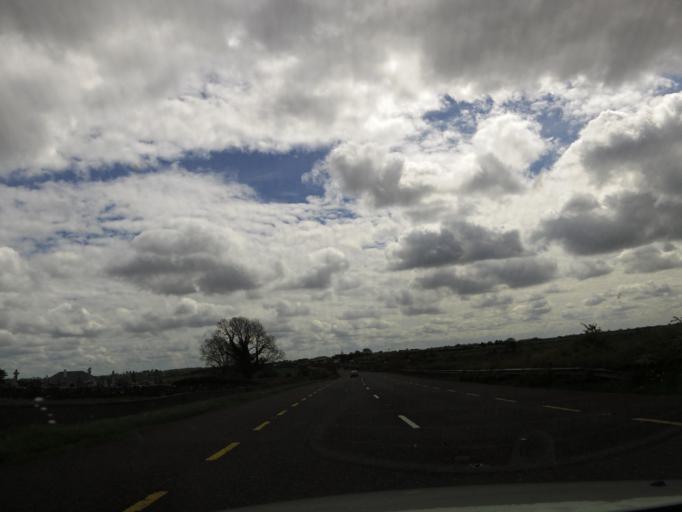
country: IE
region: Connaught
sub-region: County Galway
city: Tuam
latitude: 53.5904
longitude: -8.8665
